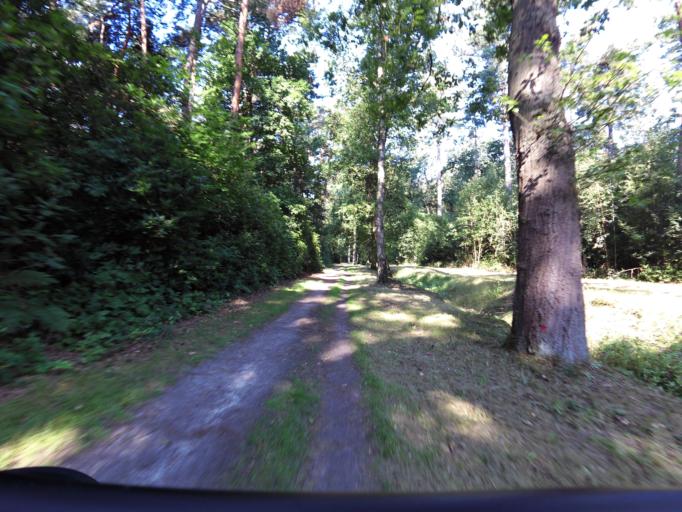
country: BE
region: Flanders
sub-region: Provincie Antwerpen
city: Stabroek
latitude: 51.3589
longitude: 4.3728
